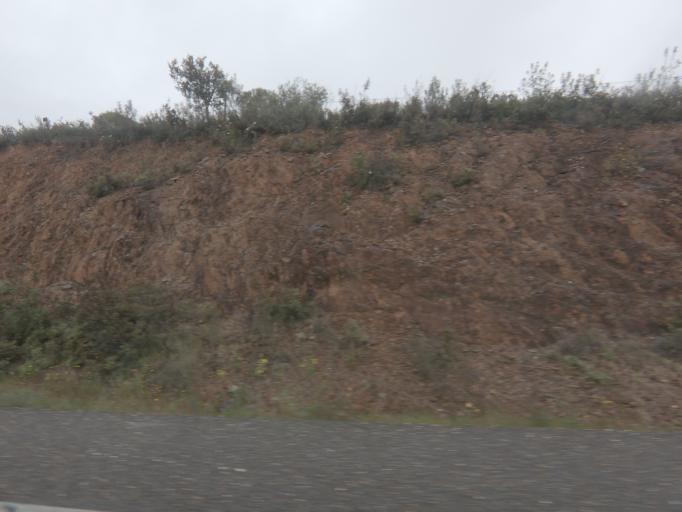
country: ES
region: Extremadura
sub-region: Provincia de Badajoz
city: Puebla de Obando
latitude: 39.1648
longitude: -6.6357
